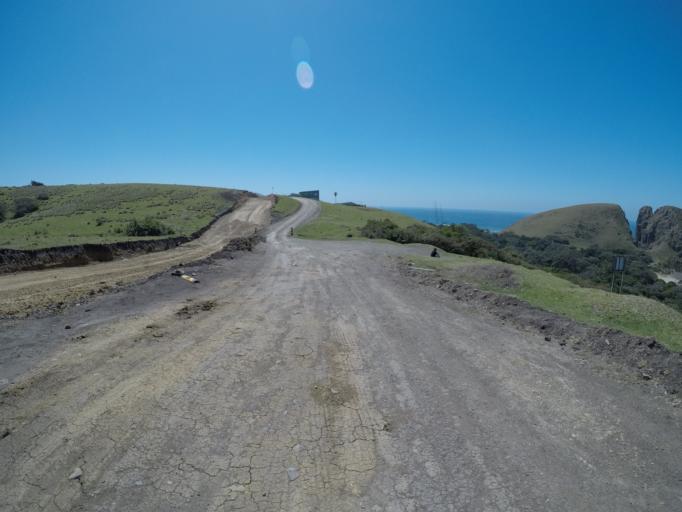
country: ZA
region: Eastern Cape
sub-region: OR Tambo District Municipality
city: Libode
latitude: -32.0381
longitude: 29.1075
